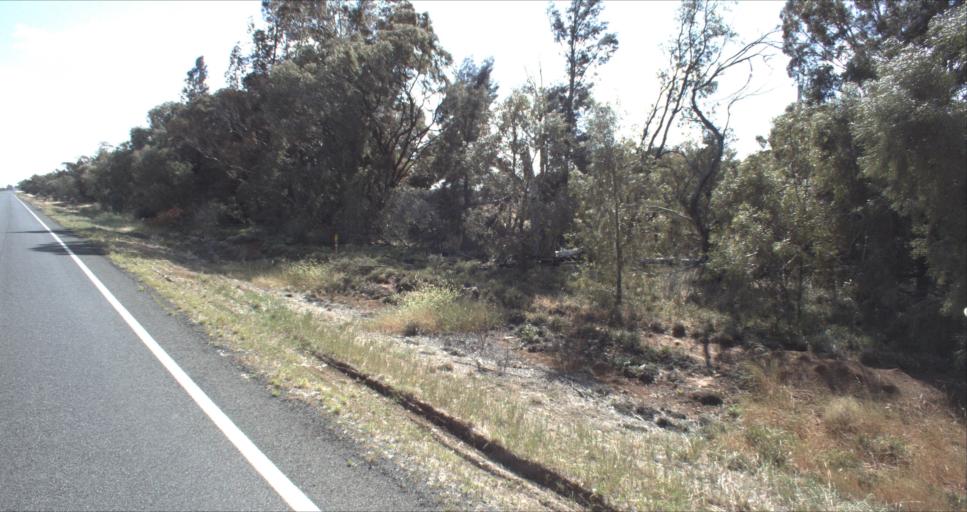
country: AU
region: New South Wales
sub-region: Murrumbidgee Shire
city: Darlington Point
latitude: -34.5292
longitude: 146.1743
